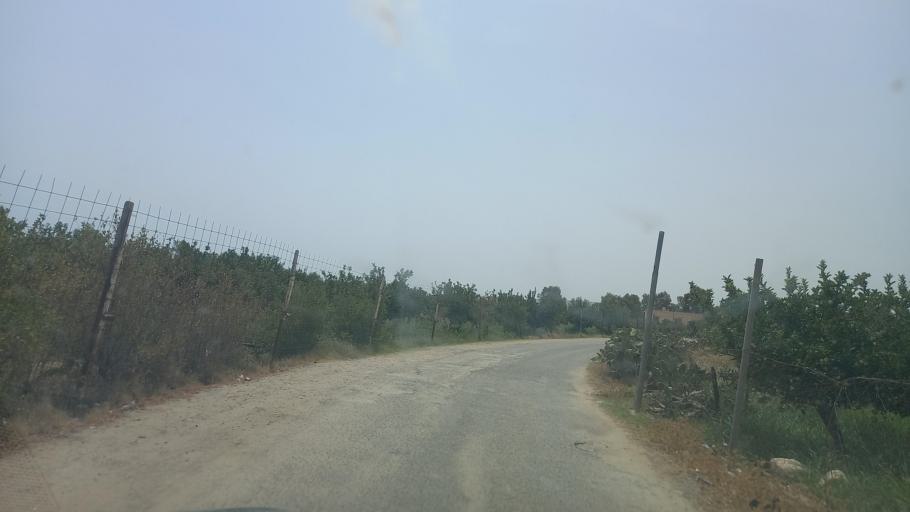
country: TN
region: Al Qasrayn
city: Kasserine
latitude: 35.2483
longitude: 9.0280
